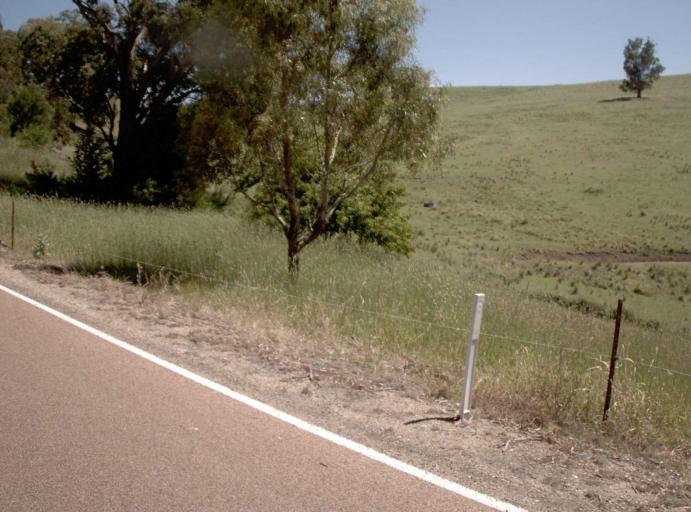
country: AU
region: Victoria
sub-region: East Gippsland
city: Lakes Entrance
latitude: -37.4809
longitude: 148.1834
